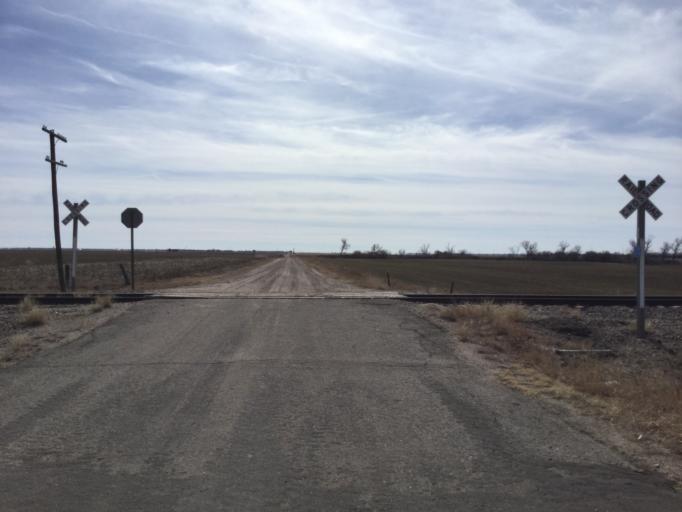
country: US
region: Kansas
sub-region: Rice County
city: Lyons
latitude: 38.5149
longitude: -98.2942
